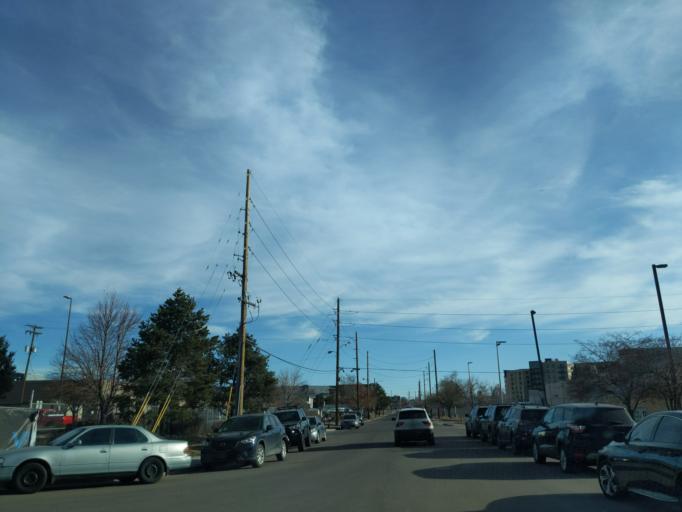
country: US
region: Colorado
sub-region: Denver County
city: Denver
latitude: 39.7696
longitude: -104.9876
